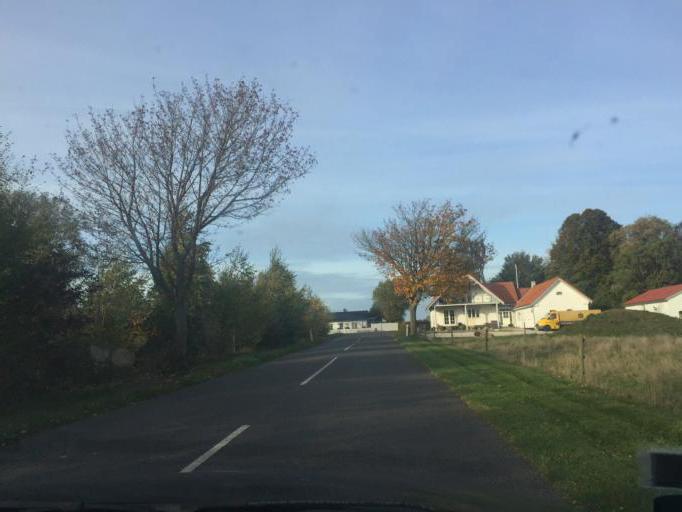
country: DK
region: Zealand
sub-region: Stevns Kommune
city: Store Heddinge
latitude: 55.2722
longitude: 12.4166
